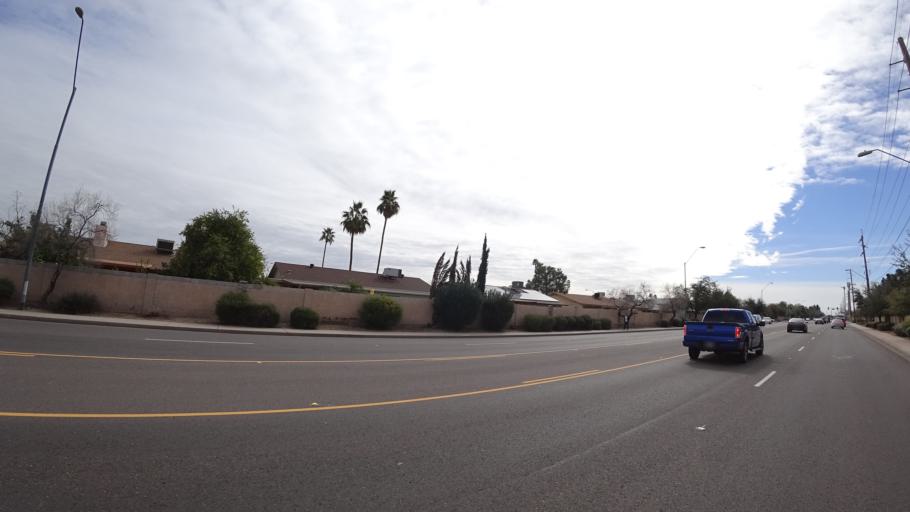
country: US
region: Arizona
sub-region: Maricopa County
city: Peoria
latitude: 33.6456
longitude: -112.1865
